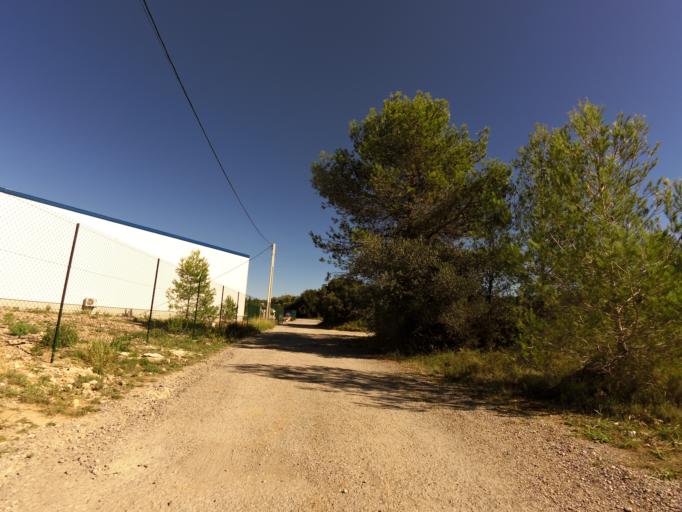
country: FR
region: Languedoc-Roussillon
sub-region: Departement de l'Herault
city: Villetelle
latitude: 43.7417
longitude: 4.1420
